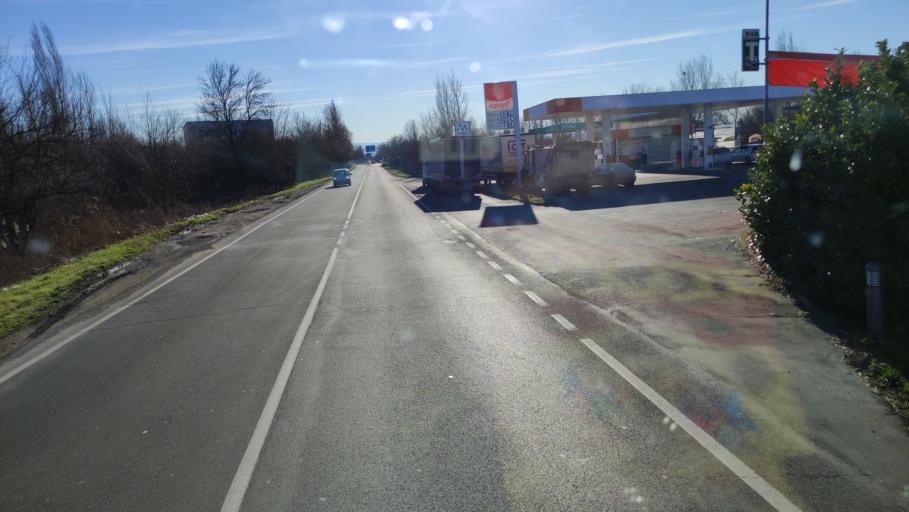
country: IT
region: Emilia-Romagna
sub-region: Provincia di Reggio Emilia
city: Bagnolo in Piano
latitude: 44.7710
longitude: 10.6672
